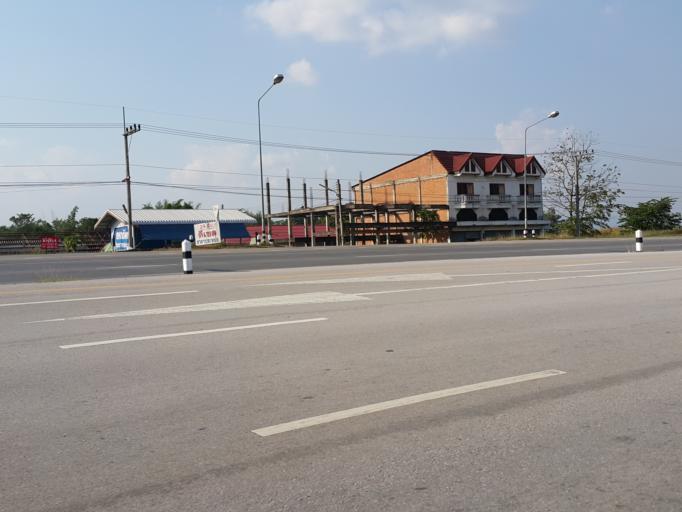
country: TH
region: Lampang
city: Thoen
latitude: 17.6404
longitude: 99.2400
